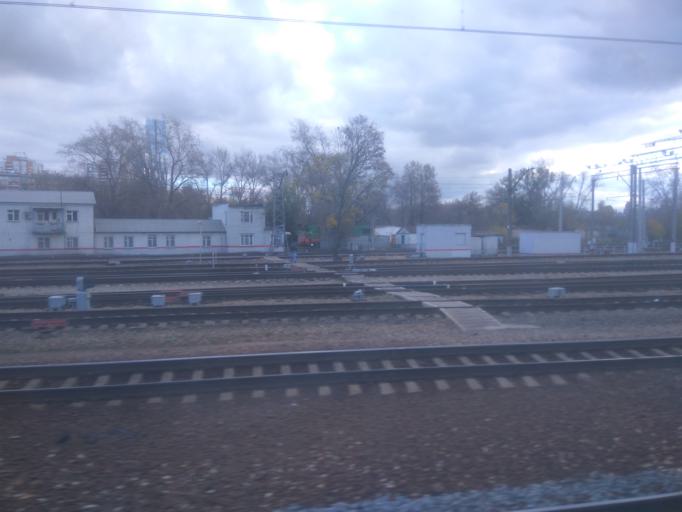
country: RU
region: Moskovskaya
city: Kastanayevo
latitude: 55.7303
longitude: 37.5158
